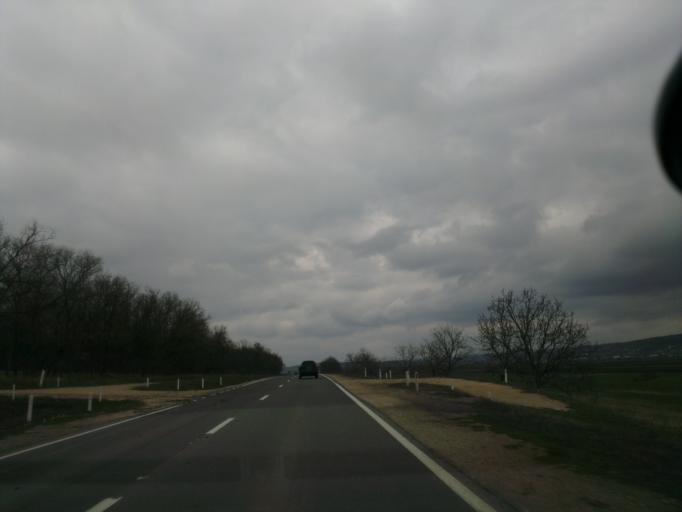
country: MD
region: Cimislia
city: Cimislia
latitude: 46.6650
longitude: 28.6980
